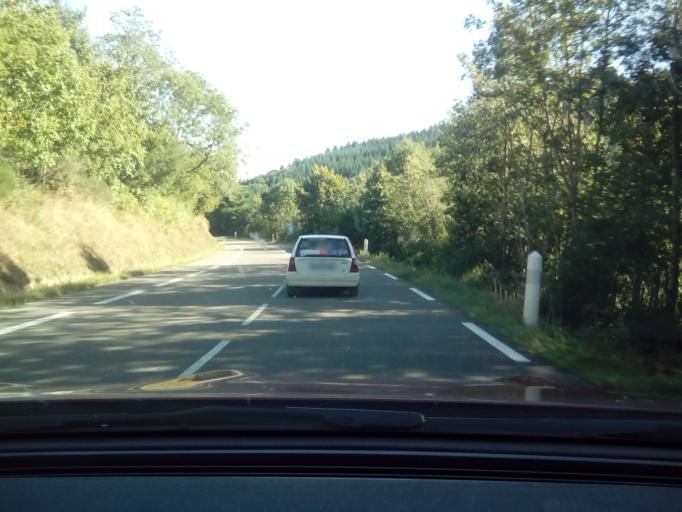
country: FR
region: Rhone-Alpes
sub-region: Departement du Rhone
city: Cublize
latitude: 45.9732
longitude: 4.4020
